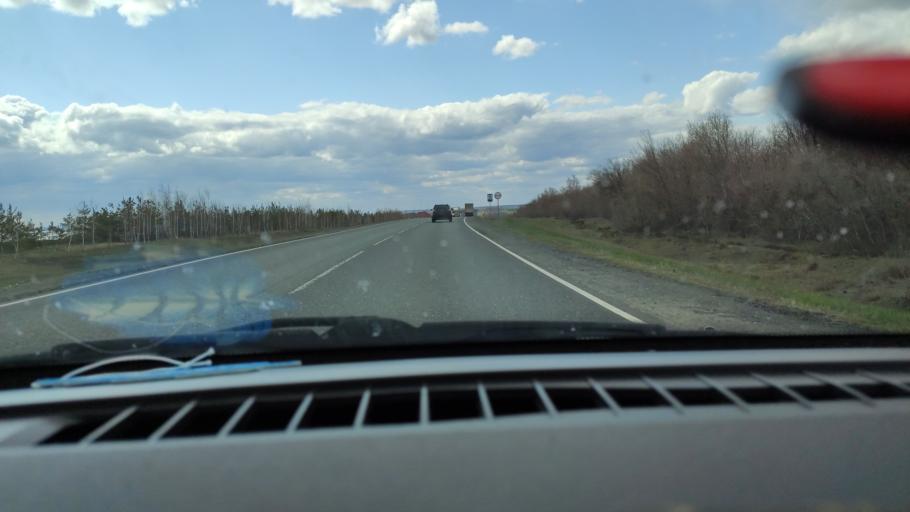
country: RU
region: Saratov
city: Balakovo
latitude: 52.1582
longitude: 47.8190
